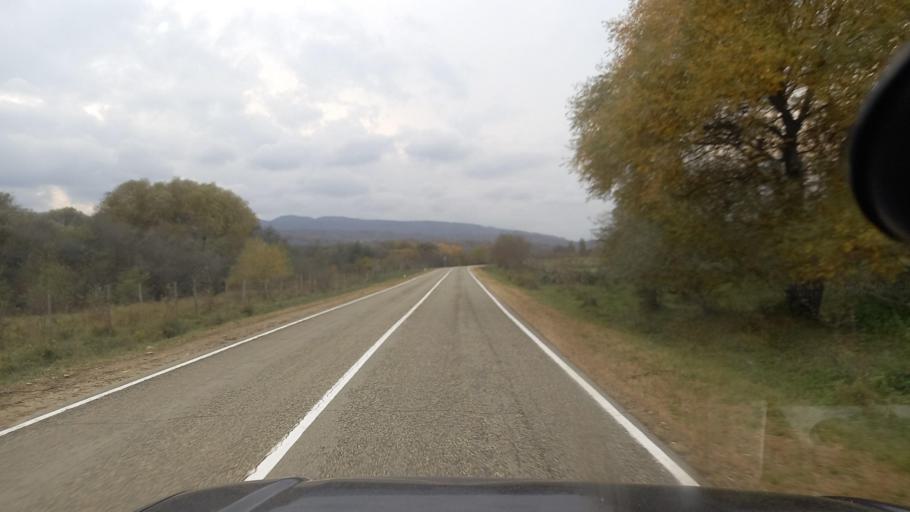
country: RU
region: Krasnodarskiy
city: Gubskaya
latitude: 44.2964
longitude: 40.5470
